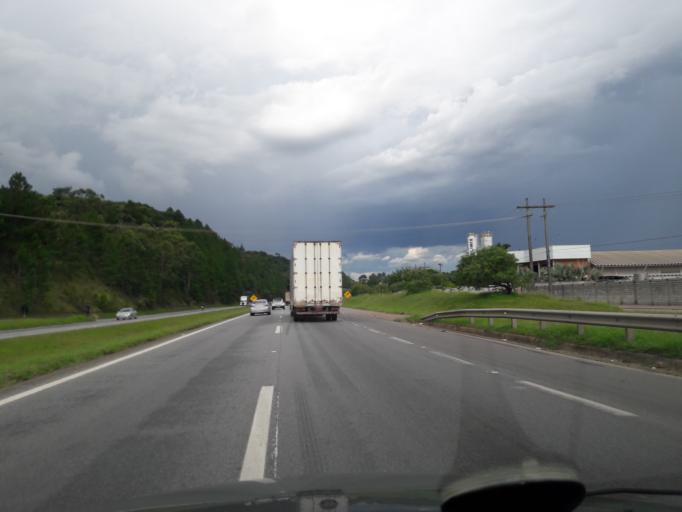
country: BR
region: Sao Paulo
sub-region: Atibaia
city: Atibaia
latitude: -23.0987
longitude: -46.5489
